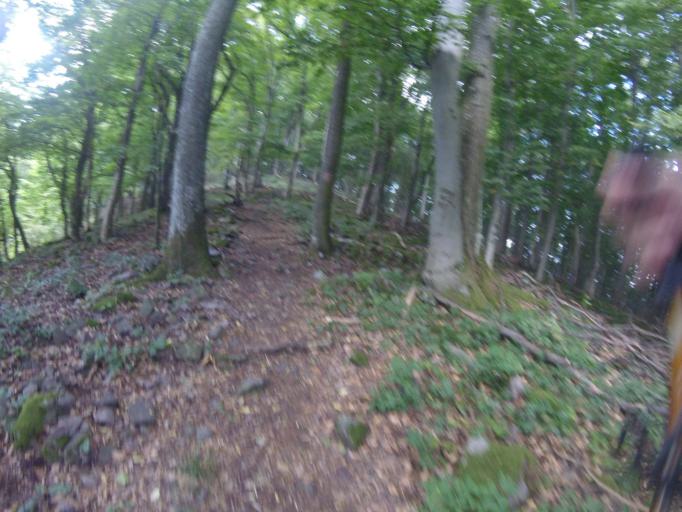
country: SK
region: Nitriansky
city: Sahy
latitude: 47.9767
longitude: 18.8862
